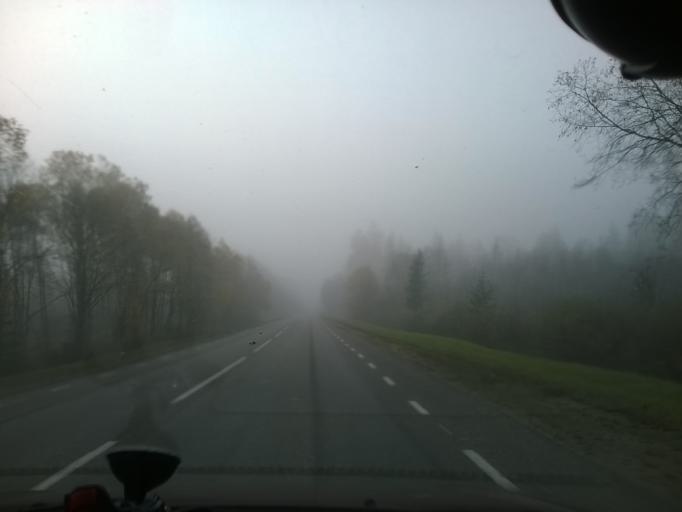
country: EE
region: Tartu
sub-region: Elva linn
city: Elva
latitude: 58.1223
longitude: 26.5180
